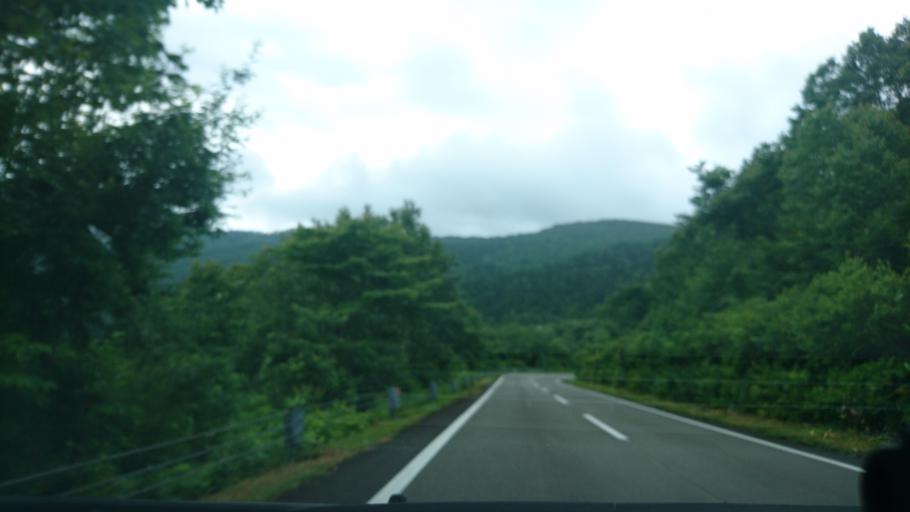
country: JP
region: Akita
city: Yuzawa
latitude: 39.1554
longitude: 140.7523
